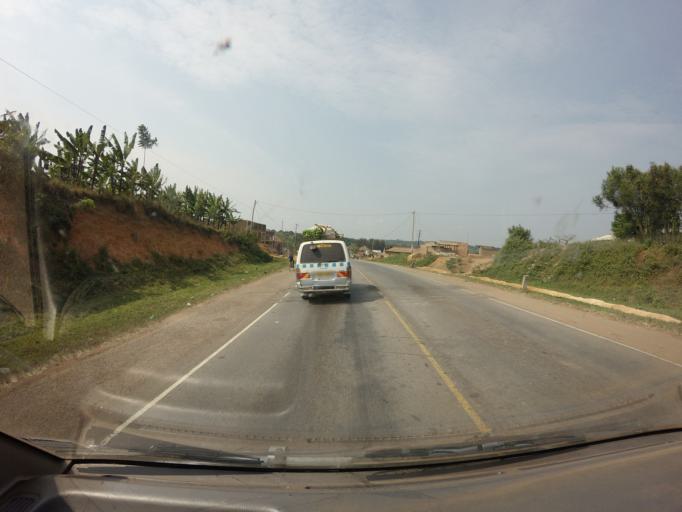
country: UG
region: Central Region
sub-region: Lwengo District
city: Lwengo
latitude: -0.3981
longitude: 31.4069
